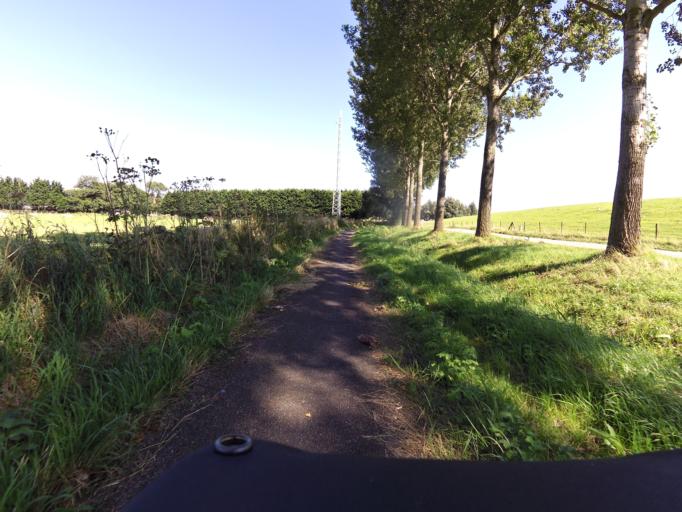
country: NL
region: South Holland
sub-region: Gemeente Dordrecht
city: Dordrecht
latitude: 51.7527
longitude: 4.7175
